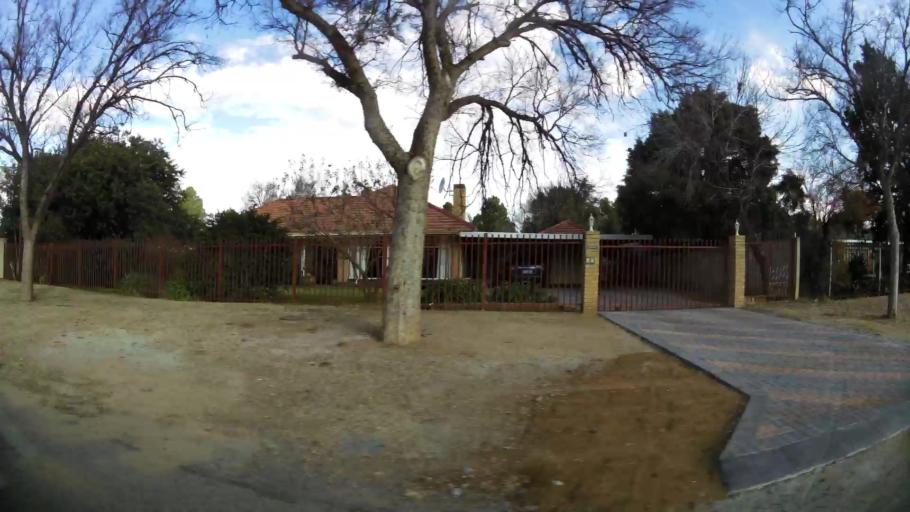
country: ZA
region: Orange Free State
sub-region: Lejweleputswa District Municipality
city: Welkom
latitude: -27.9867
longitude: 26.7213
